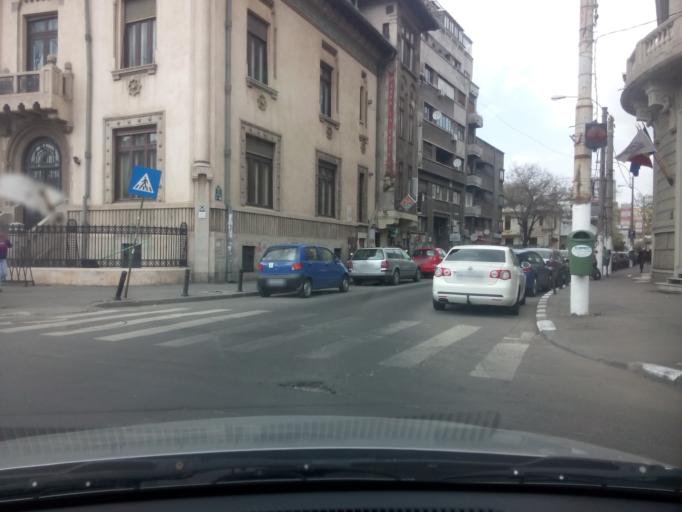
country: RO
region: Bucuresti
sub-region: Municipiul Bucuresti
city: Bucharest
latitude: 44.4474
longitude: 26.0966
